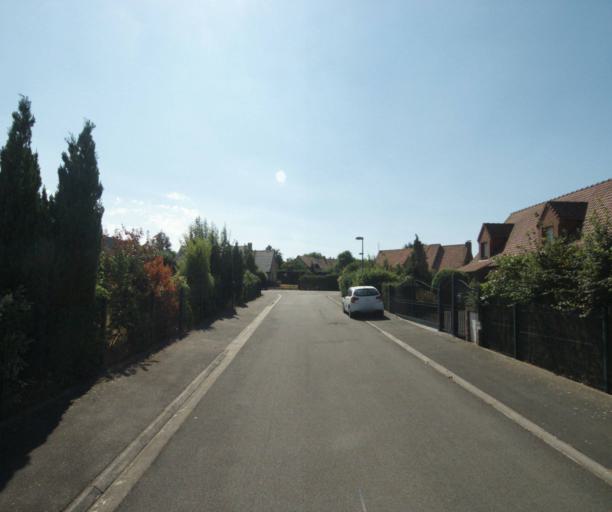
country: FR
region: Nord-Pas-de-Calais
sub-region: Departement du Nord
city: Halluin
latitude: 50.7779
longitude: 3.1405
